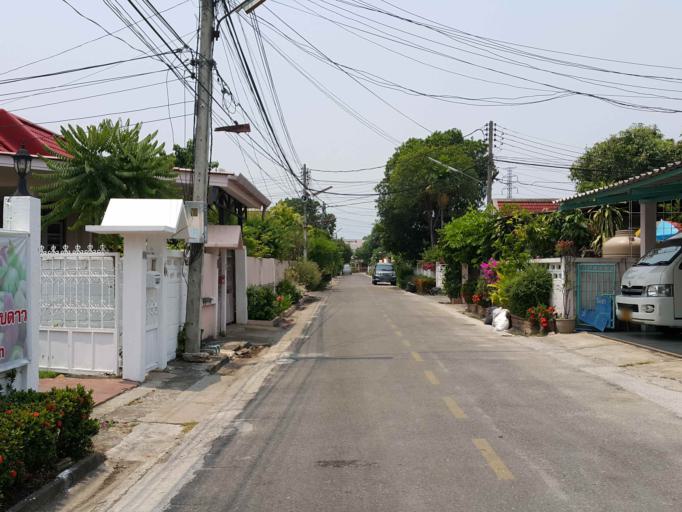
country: TH
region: Chiang Mai
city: Chiang Mai
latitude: 18.7547
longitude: 99.0117
